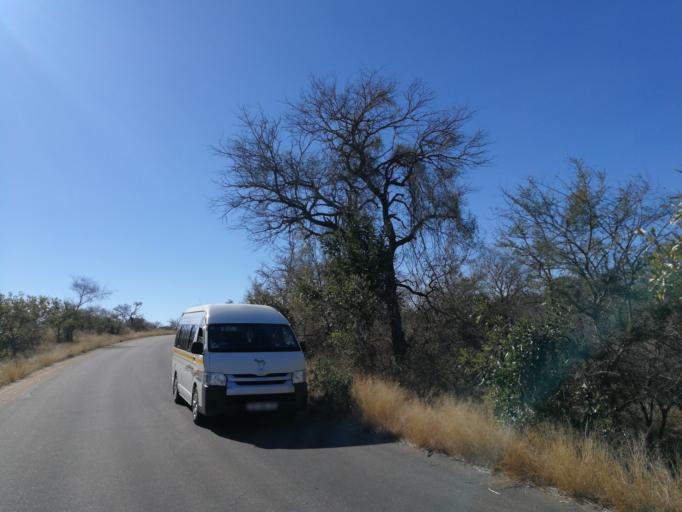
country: ZA
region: Mpumalanga
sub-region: Ehlanzeni District
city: Komatipoort
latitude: -24.9931
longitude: 31.7669
